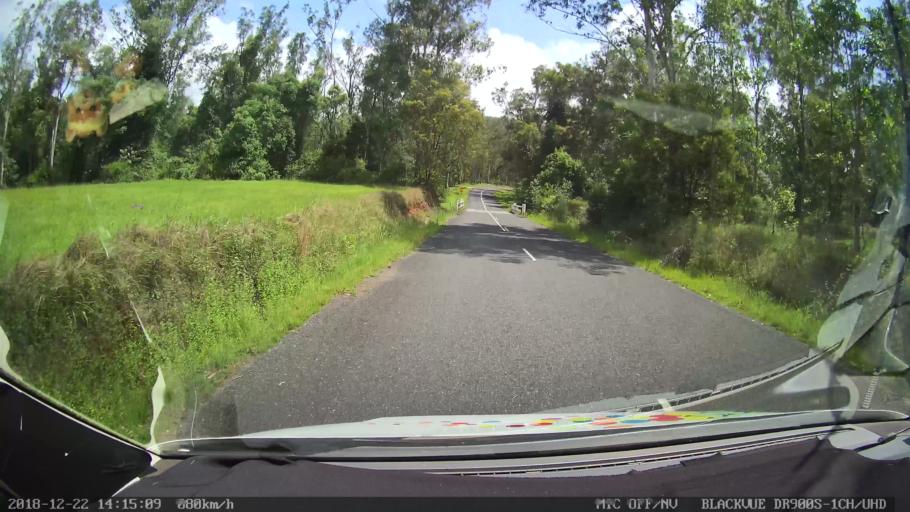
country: AU
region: New South Wales
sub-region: Clarence Valley
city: Coutts Crossing
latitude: -30.0001
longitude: 152.6808
